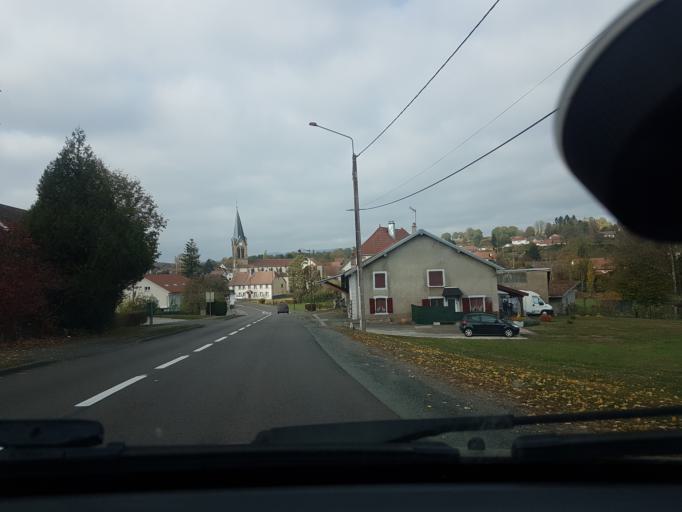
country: FR
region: Franche-Comte
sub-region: Departement de la Haute-Saone
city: Frahier-et-Chatebier
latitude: 47.6574
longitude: 6.7498
